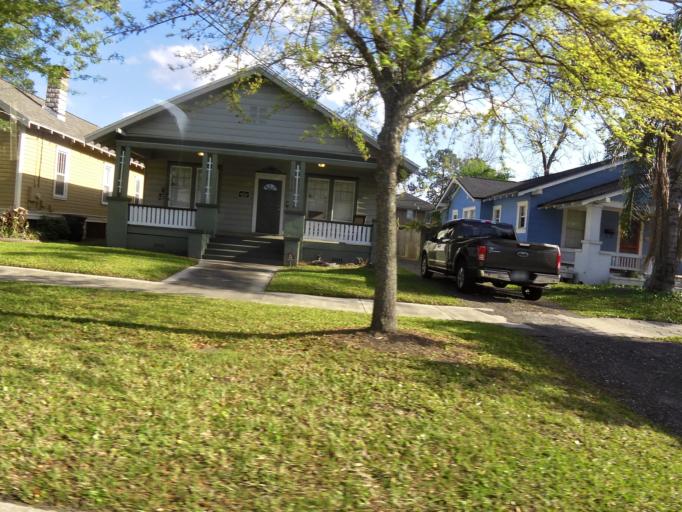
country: US
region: Florida
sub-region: Duval County
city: Jacksonville
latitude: 30.3197
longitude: -81.6846
